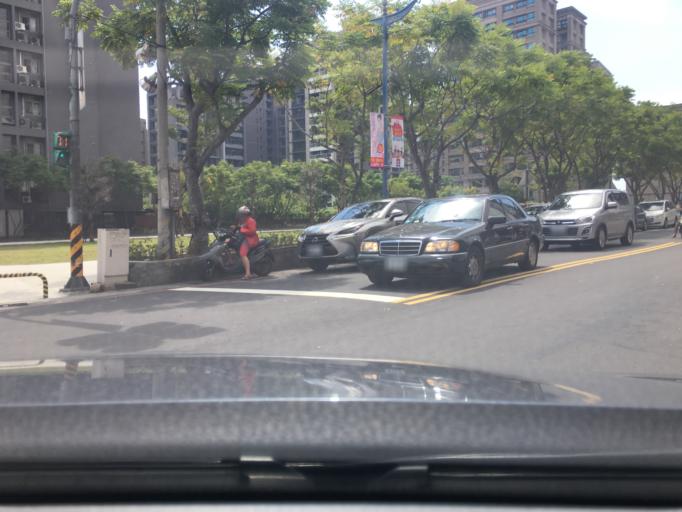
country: TW
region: Taipei
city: Taipei
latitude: 25.0879
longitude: 121.4872
